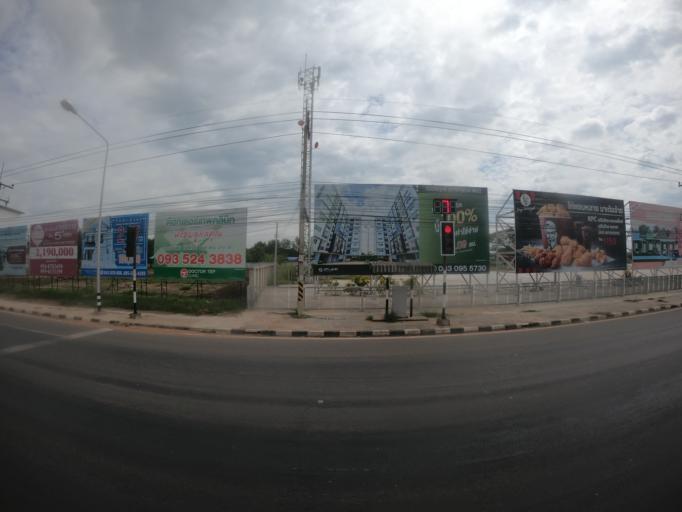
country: TH
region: Maha Sarakham
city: Maha Sarakham
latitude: 16.2474
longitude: 103.2738
